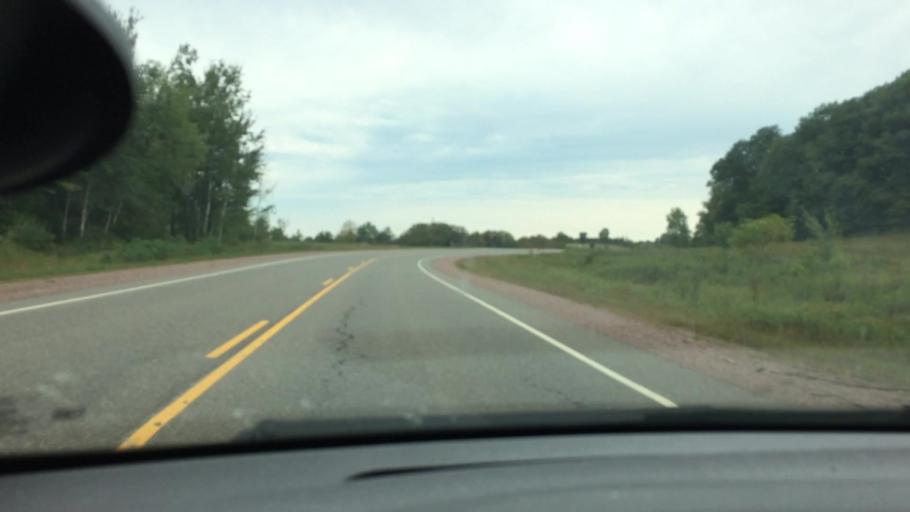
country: US
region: Wisconsin
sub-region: Clark County
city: Neillsville
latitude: 44.5534
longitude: -90.6357
